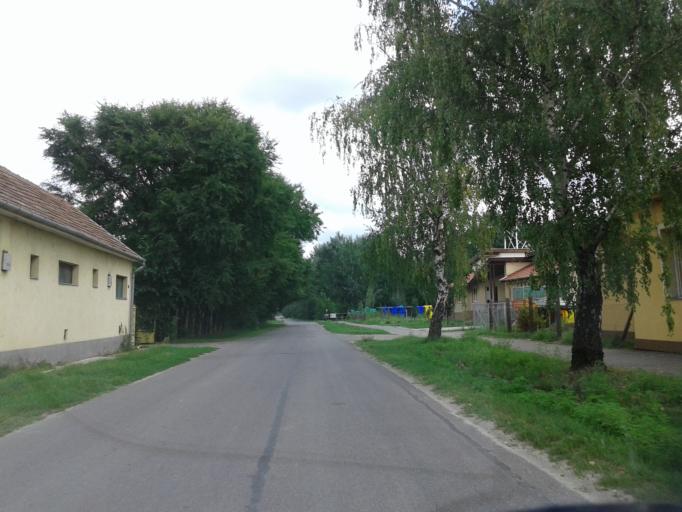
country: HU
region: Csongrad
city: Morahalom
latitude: 46.2128
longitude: 19.8915
